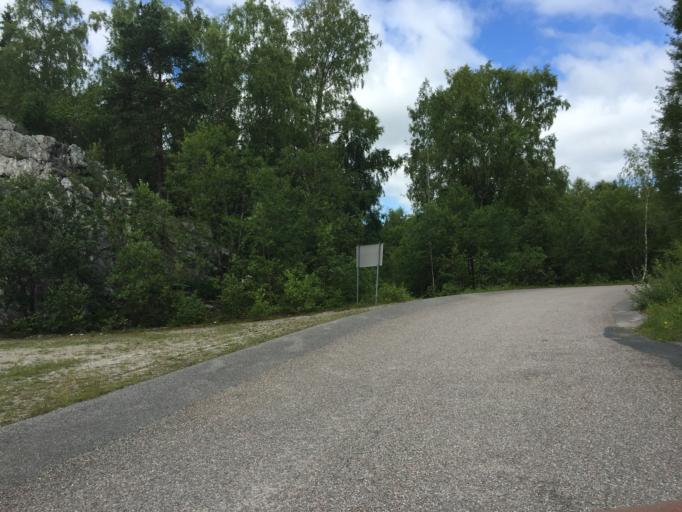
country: SE
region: Stockholm
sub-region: Nynashamns Kommun
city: Osmo
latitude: 58.9748
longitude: 17.7160
